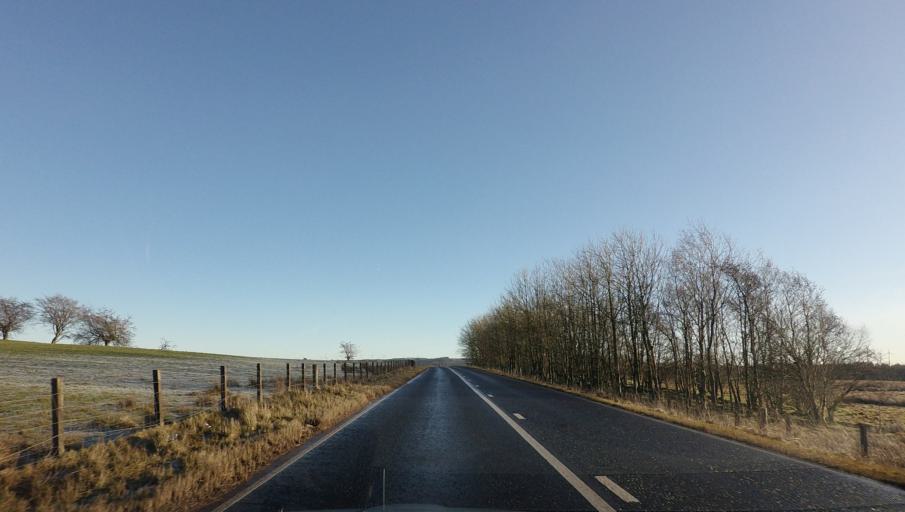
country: GB
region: Scotland
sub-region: North Lanarkshire
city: Shotts
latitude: 55.8055
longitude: -3.7679
